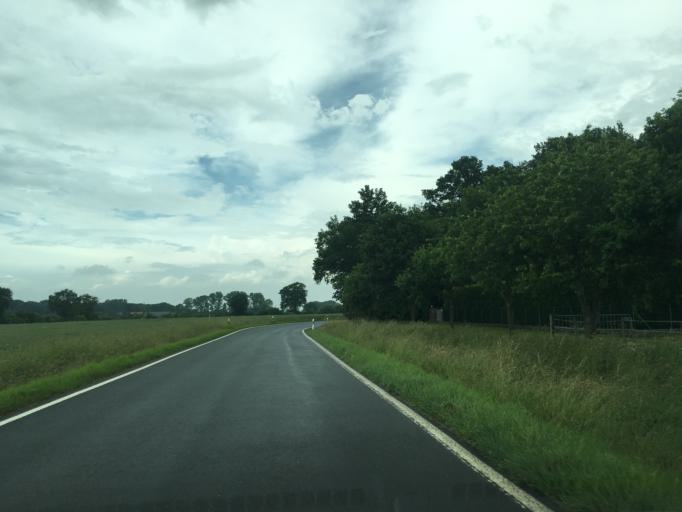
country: DE
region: North Rhine-Westphalia
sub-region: Regierungsbezirk Munster
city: Altenberge
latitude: 52.0051
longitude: 7.4665
